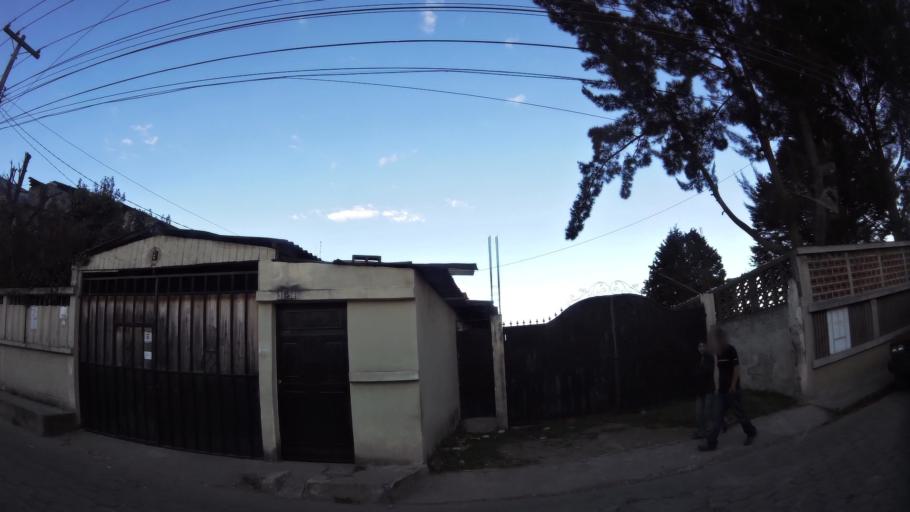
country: GT
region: Quetzaltenango
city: Quetzaltenango
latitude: 14.8566
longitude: -91.5336
